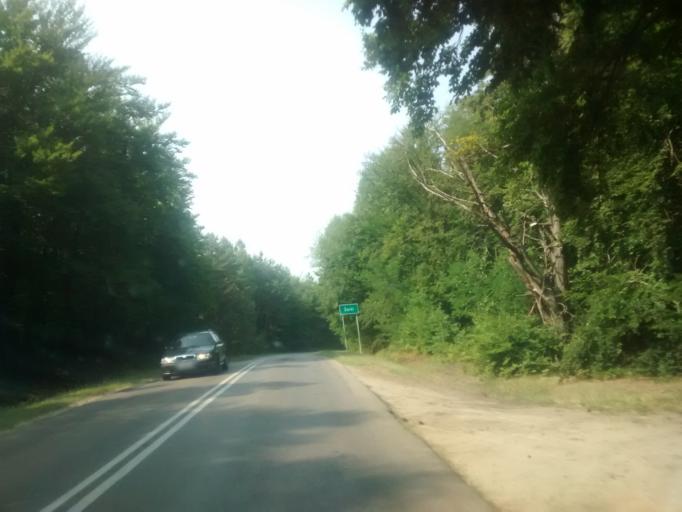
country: PL
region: Silesian Voivodeship
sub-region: Powiat myszkowski
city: Zarki
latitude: 50.6344
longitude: 19.4292
